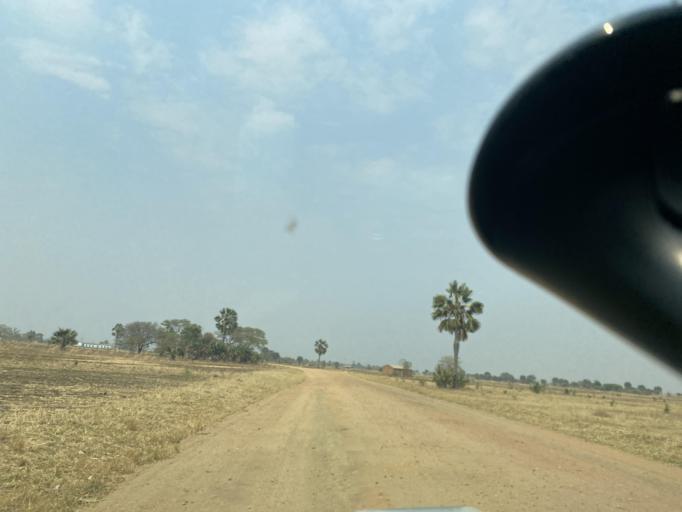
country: ZM
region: Lusaka
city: Kafue
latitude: -15.6487
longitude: 28.0328
